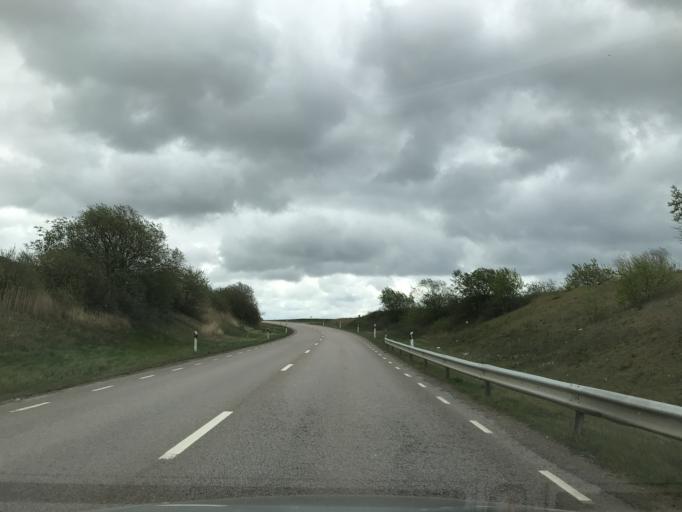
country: SE
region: Skane
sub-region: Helsingborg
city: Glumslov
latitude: 55.9556
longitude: 12.7947
